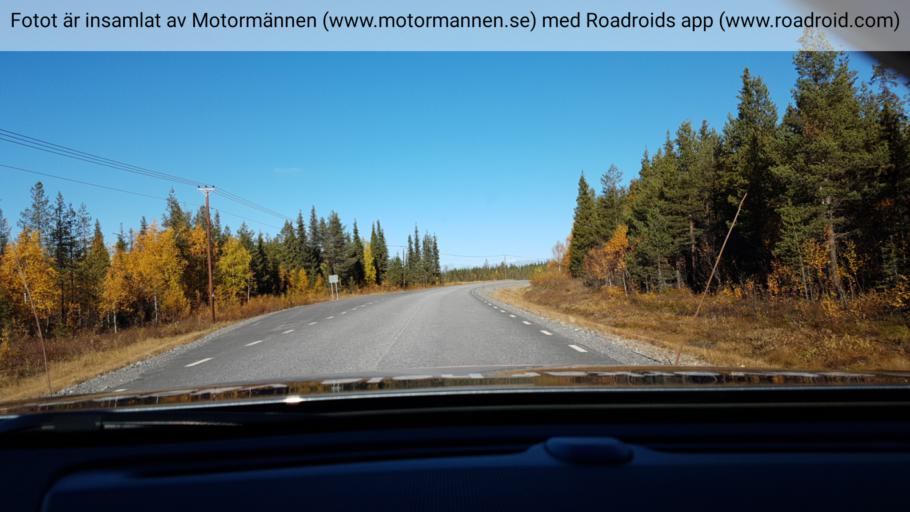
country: SE
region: Norrbotten
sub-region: Gallivare Kommun
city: Gaellivare
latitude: 66.8035
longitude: 21.0381
